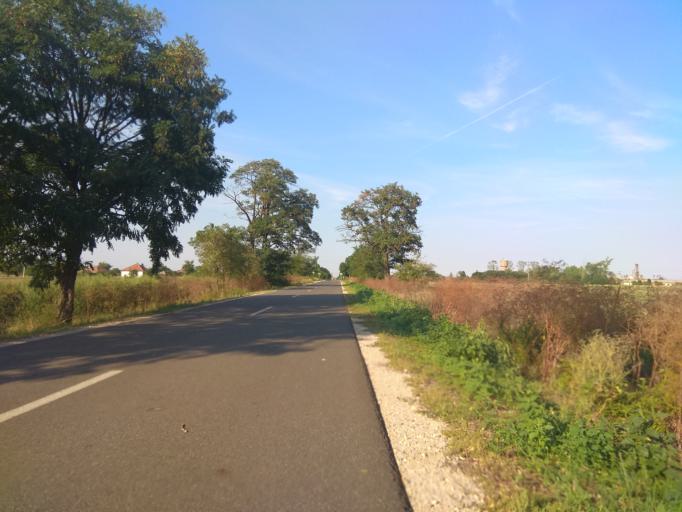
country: HU
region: Borsod-Abauj-Zemplen
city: Emod
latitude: 47.8824
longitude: 20.7675
